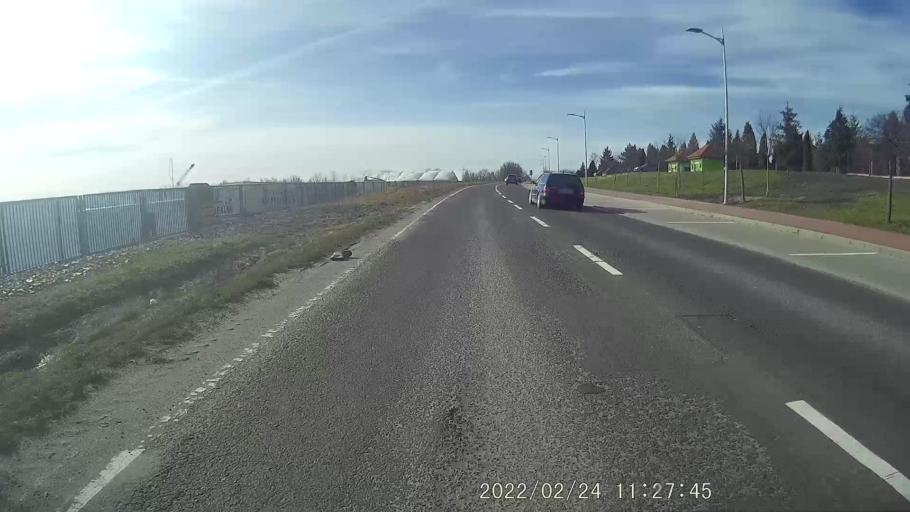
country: PL
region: Lower Silesian Voivodeship
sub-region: Powiat polkowicki
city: Przemkow
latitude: 51.5332
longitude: 15.6678
